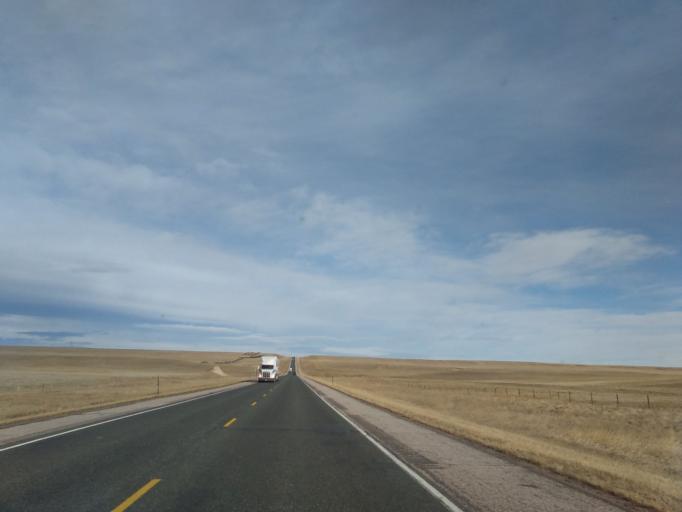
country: US
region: Wyoming
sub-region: Laramie County
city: Pine Bluffs
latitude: 41.5790
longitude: -104.2723
